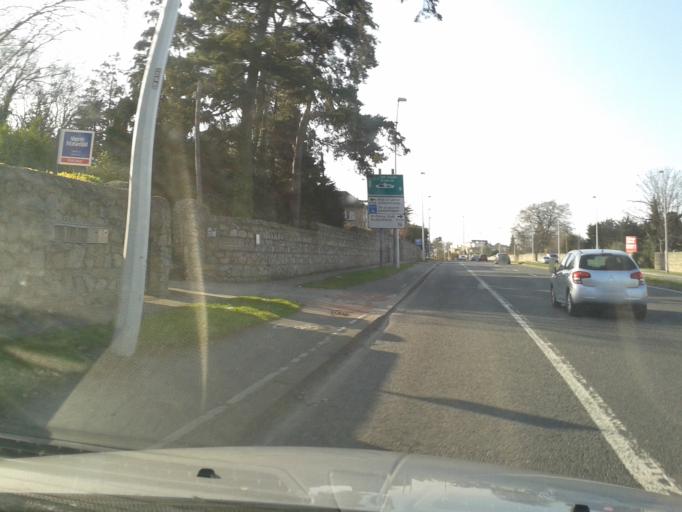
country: IE
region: Leinster
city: Foxrock
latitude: 53.2761
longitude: -6.1808
